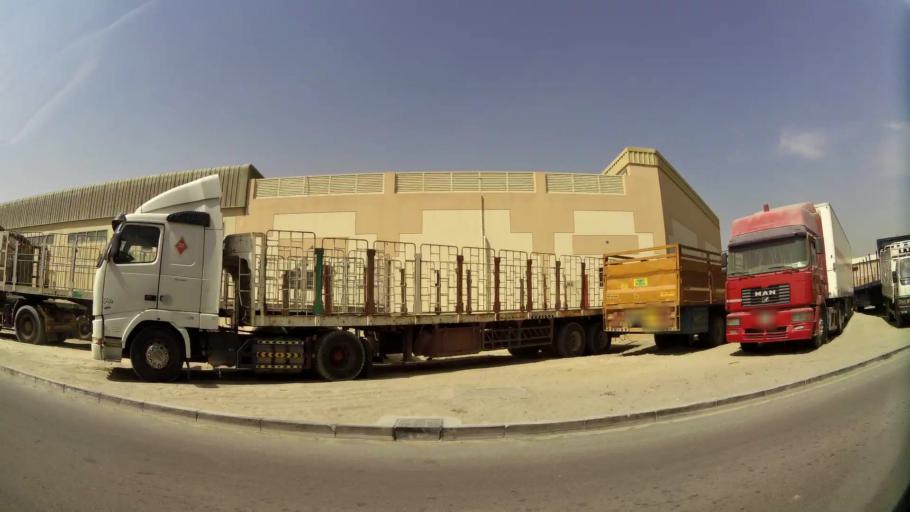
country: AE
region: Ash Shariqah
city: Sharjah
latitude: 25.2763
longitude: 55.3901
